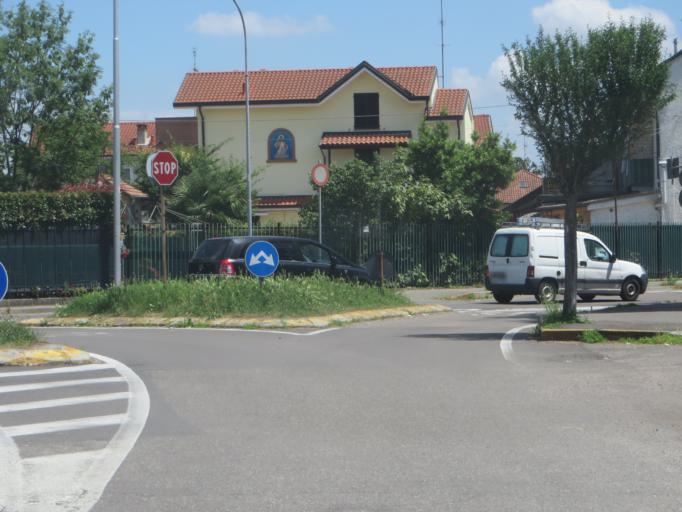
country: IT
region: Lombardy
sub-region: Citta metropolitana di Milano
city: Bareggio
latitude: 45.4784
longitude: 8.9914
